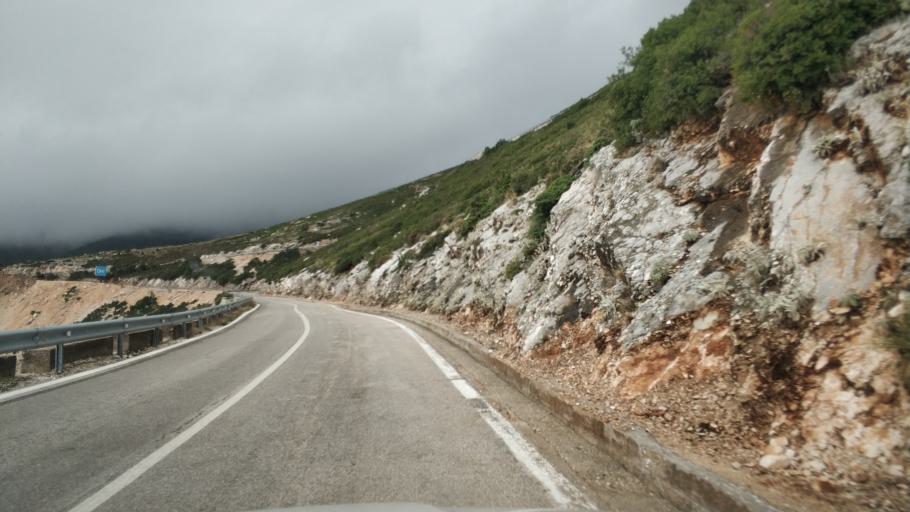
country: AL
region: Vlore
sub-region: Rrethi i Vlores
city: Vranisht
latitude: 40.1837
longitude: 19.5964
